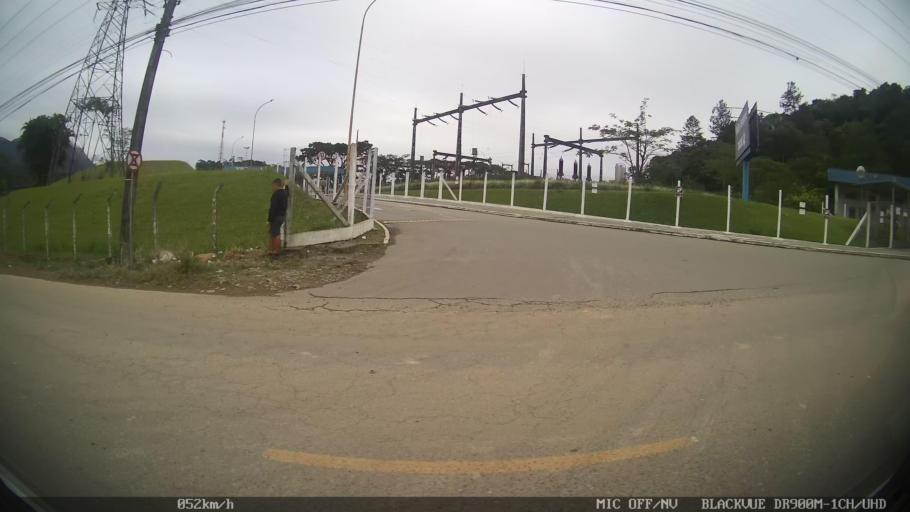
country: BR
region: Santa Catarina
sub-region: Joinville
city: Joinville
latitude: -26.2515
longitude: -48.9130
